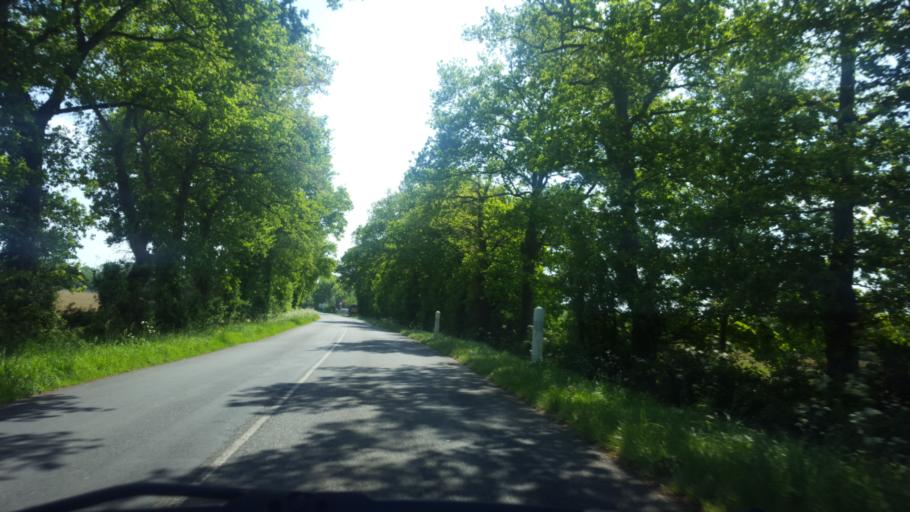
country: FR
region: Pays de la Loire
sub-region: Departement de la Loire-Atlantique
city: La Limouziniere
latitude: 46.9753
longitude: -1.5715
